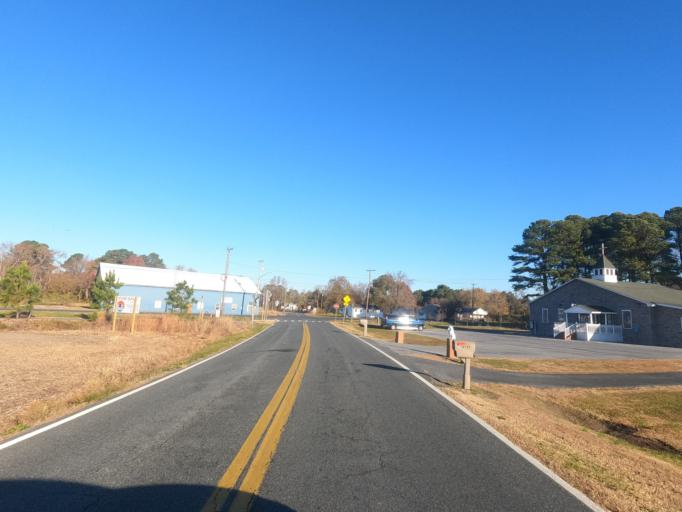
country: US
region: Maryland
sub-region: Somerset County
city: Crisfield
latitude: 38.0095
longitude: -75.8154
